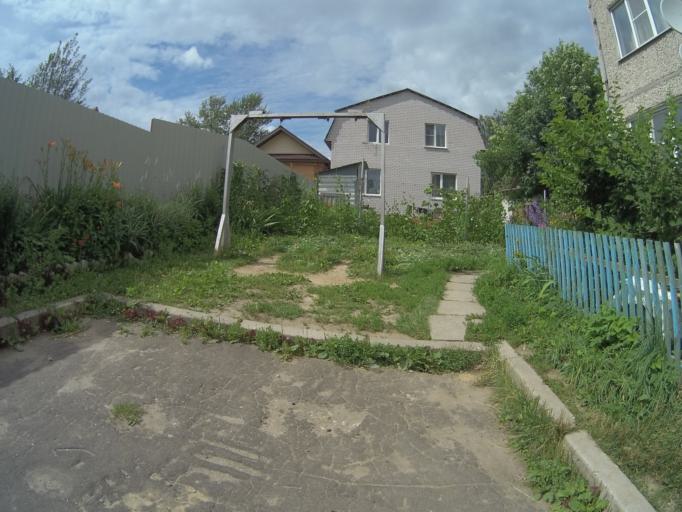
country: RU
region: Vladimir
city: Bogolyubovo
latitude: 56.2124
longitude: 40.5226
